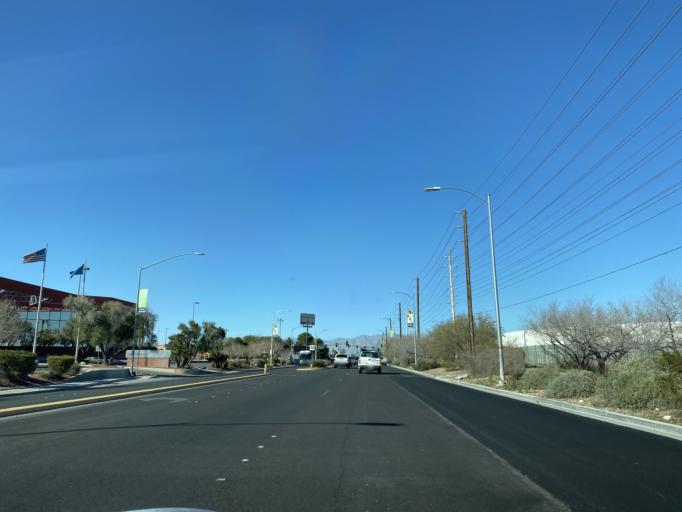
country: US
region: Nevada
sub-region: Clark County
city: Las Vegas
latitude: 36.1682
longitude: -115.1925
